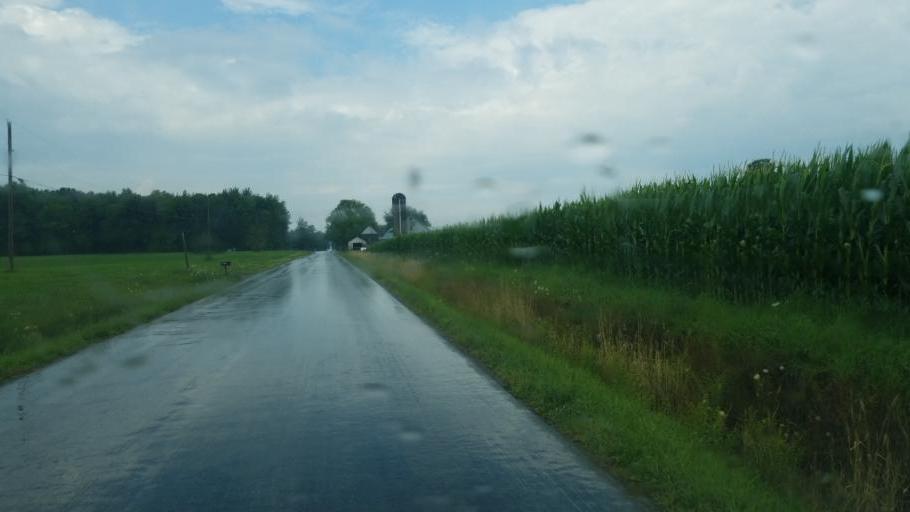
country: US
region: Ohio
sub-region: Geauga County
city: Middlefield
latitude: 41.4761
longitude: -80.9789
